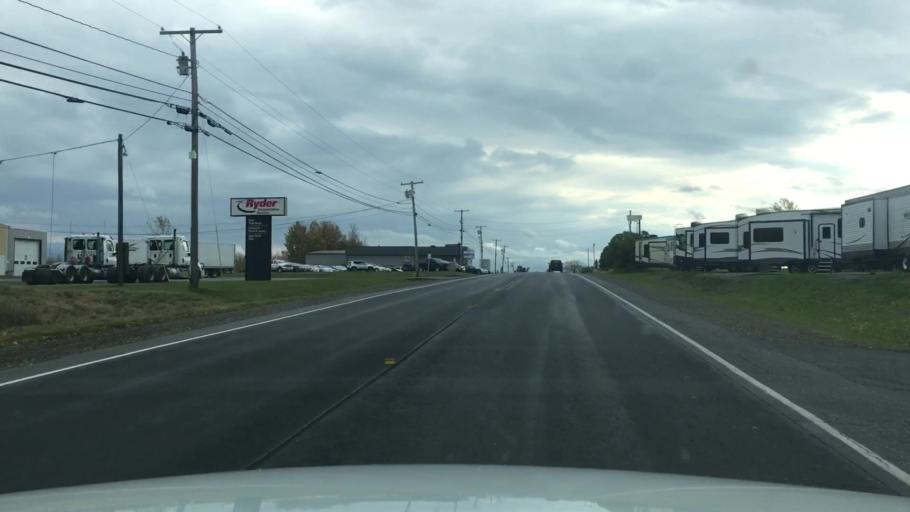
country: US
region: Maine
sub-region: Aroostook County
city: Presque Isle
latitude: 46.6600
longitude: -68.0078
